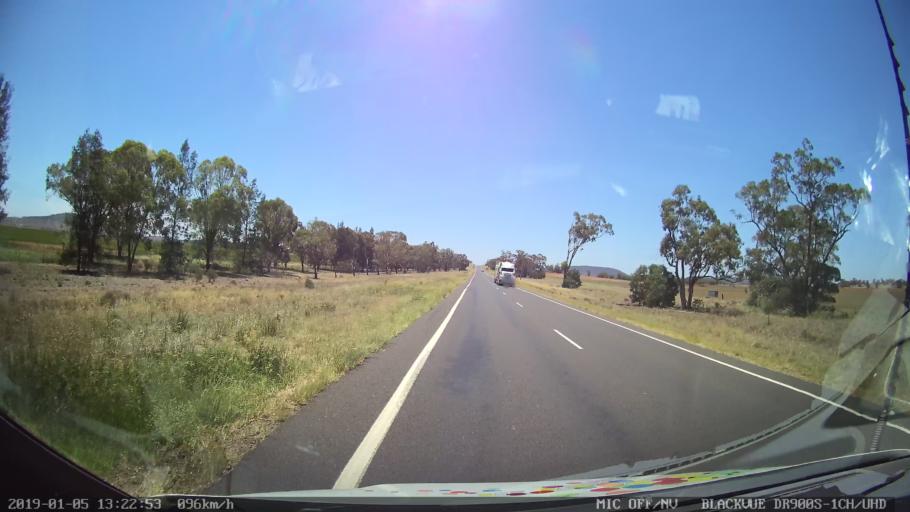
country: AU
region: New South Wales
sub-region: Gunnedah
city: Gunnedah
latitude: -31.0824
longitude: 149.9679
